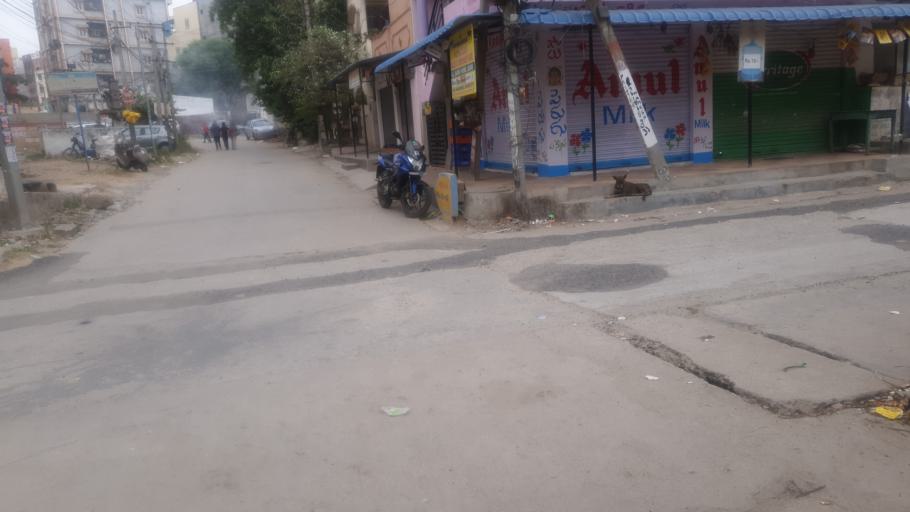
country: IN
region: Telangana
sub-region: Rangareddi
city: Kukatpalli
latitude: 17.4919
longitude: 78.3582
